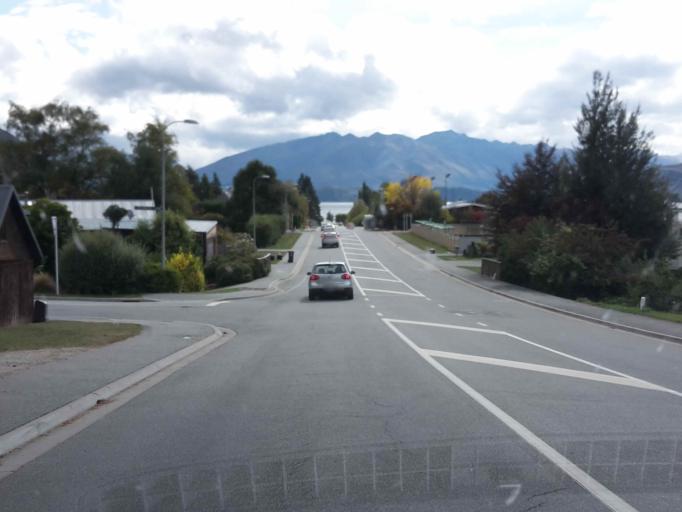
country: NZ
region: Otago
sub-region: Queenstown-Lakes District
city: Wanaka
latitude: -44.7042
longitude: 169.1332
